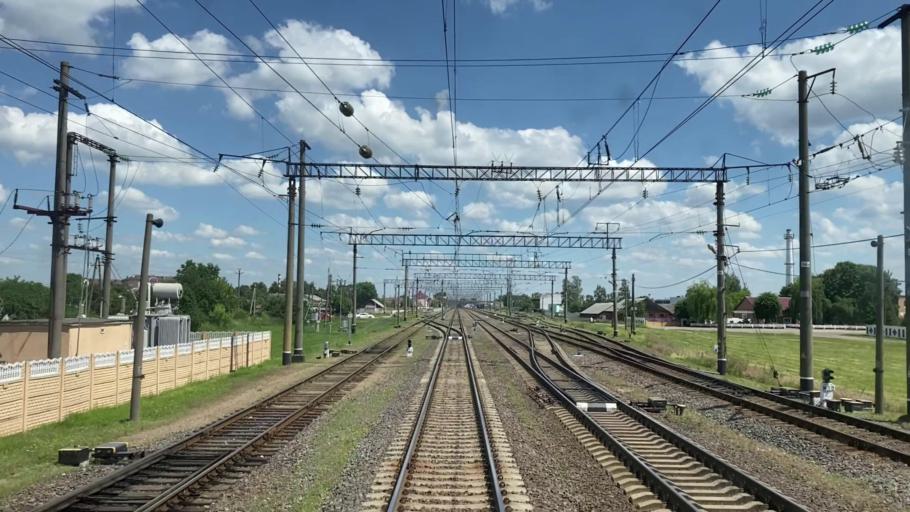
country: BY
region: Brest
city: Ivatsevichy
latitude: 52.7041
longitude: 25.3335
